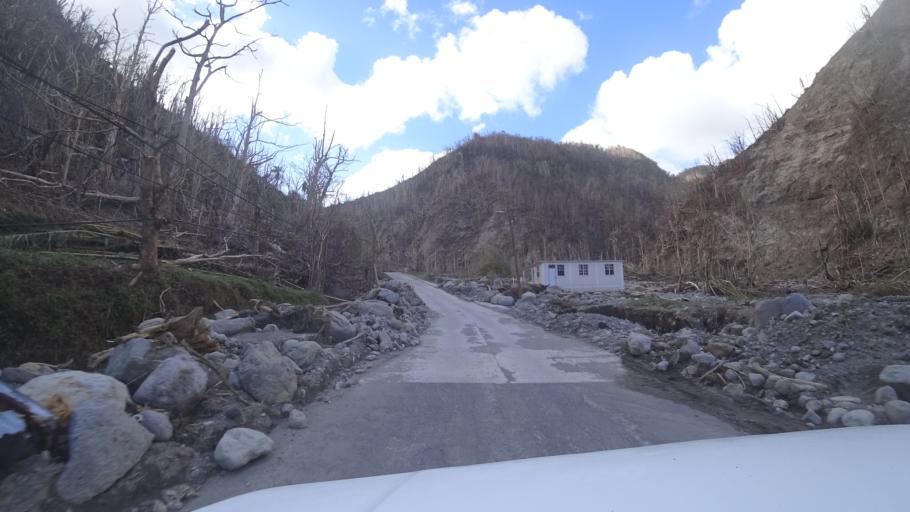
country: DM
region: Saint Patrick
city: Berekua
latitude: 15.2630
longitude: -61.3199
